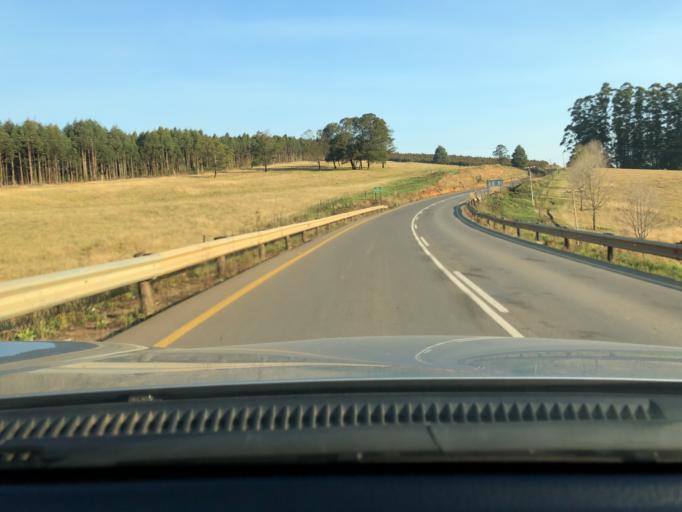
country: ZA
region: KwaZulu-Natal
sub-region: Sisonke District Municipality
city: Ixopo
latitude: -30.1680
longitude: 30.0626
